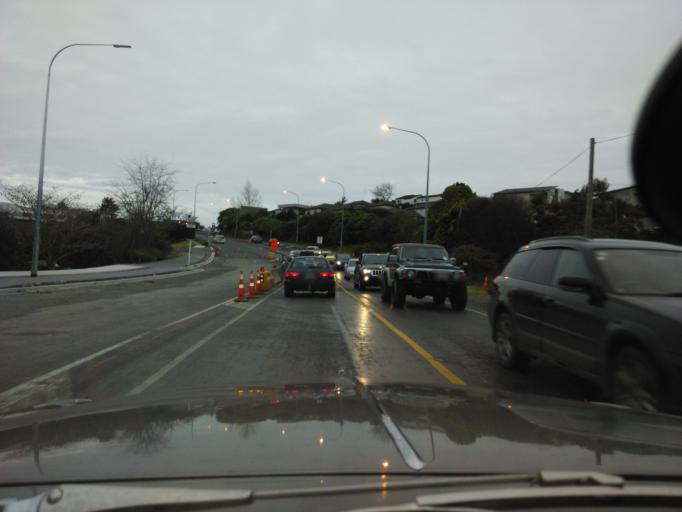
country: NZ
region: Auckland
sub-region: Auckland
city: Rothesay Bay
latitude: -36.7542
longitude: 174.6986
